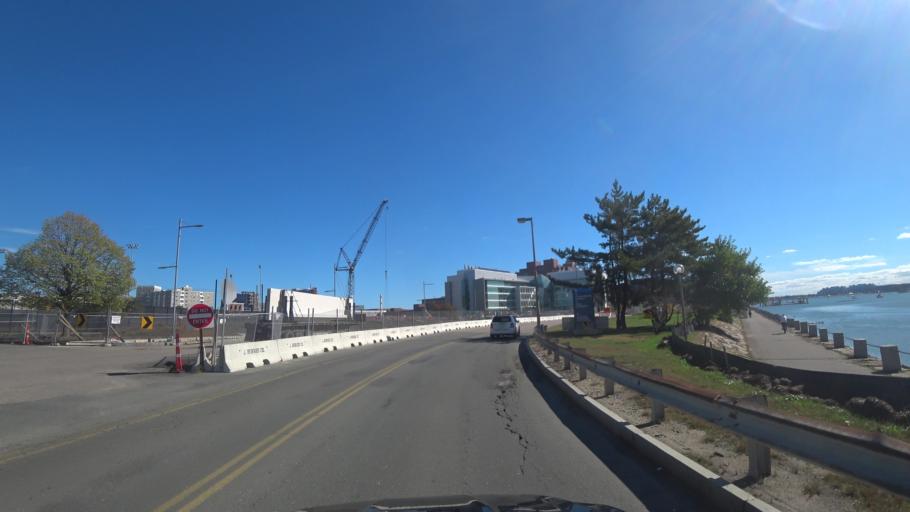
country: US
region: Massachusetts
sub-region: Suffolk County
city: South Boston
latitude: 42.3143
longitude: -71.0445
